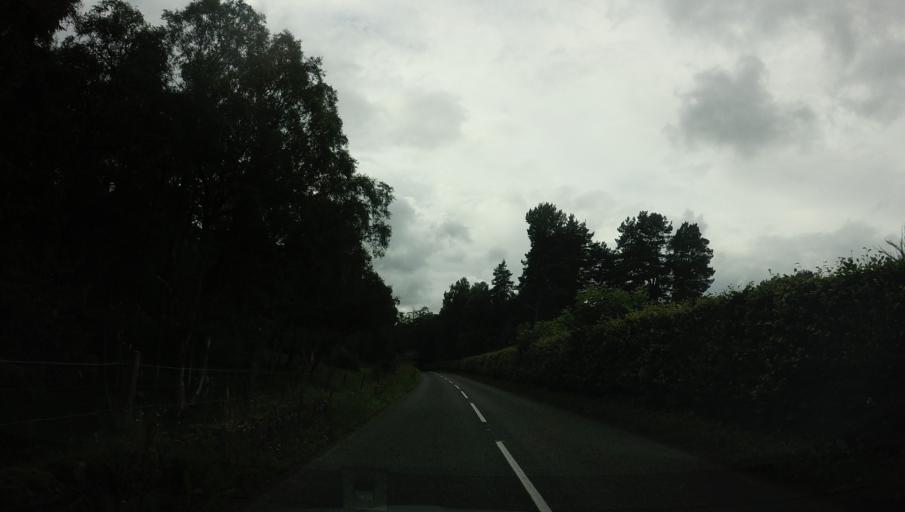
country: GB
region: Scotland
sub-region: Aberdeenshire
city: Aboyne
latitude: 57.0611
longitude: -2.7028
